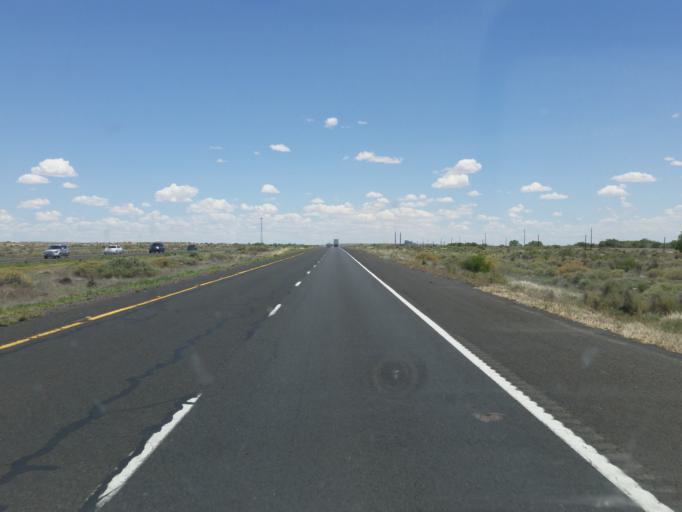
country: US
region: Arizona
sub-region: Navajo County
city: Joseph City
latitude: 34.9627
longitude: -110.3930
